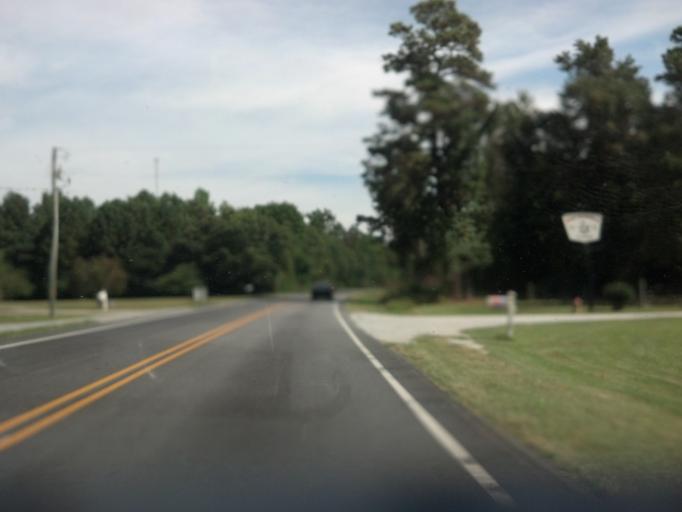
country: US
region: North Carolina
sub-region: Greene County
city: Snow Hill
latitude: 35.4781
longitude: -77.6547
